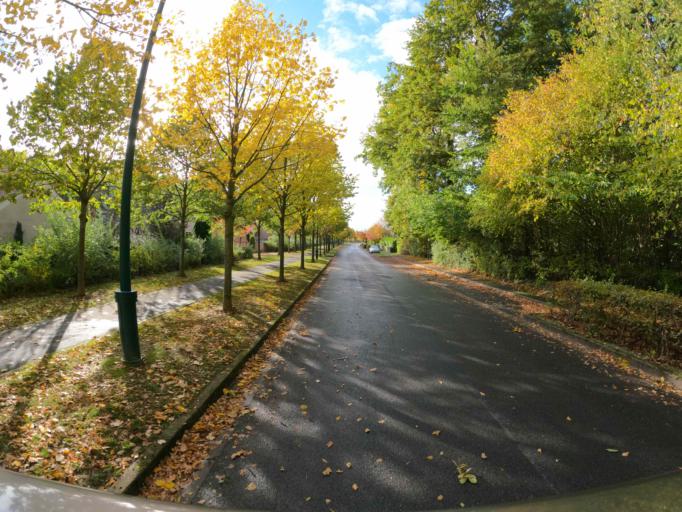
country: FR
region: Ile-de-France
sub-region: Departement de Seine-et-Marne
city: Magny-le-Hongre
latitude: 48.8656
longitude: 2.8235
